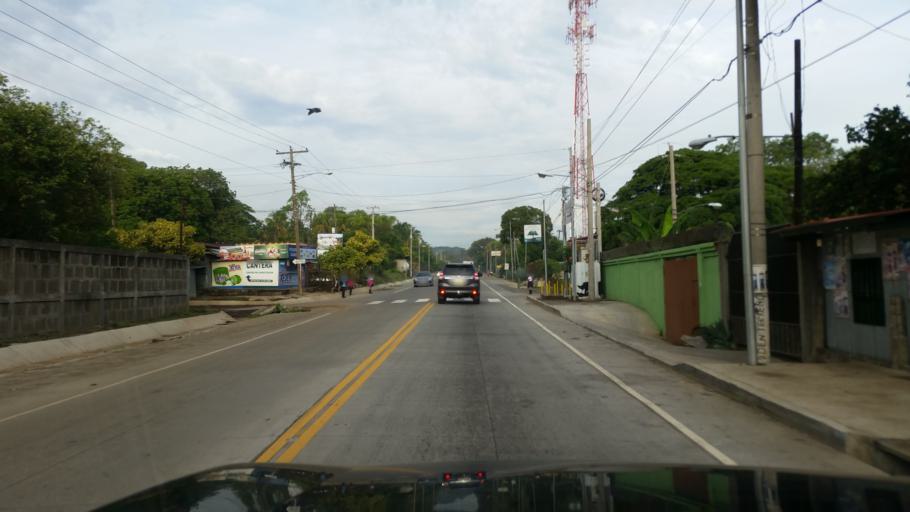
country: NI
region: Managua
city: Ciudad Sandino
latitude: 12.1020
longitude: -86.3384
